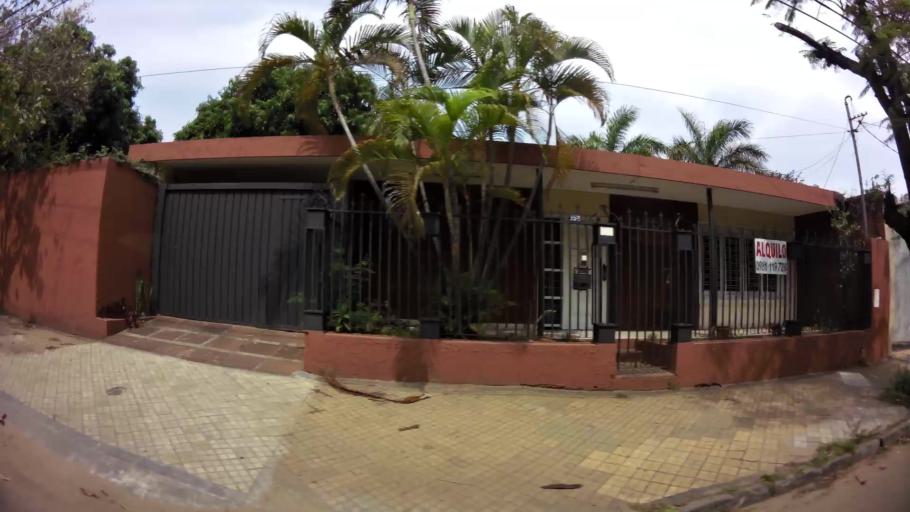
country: PY
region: Asuncion
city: Asuncion
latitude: -25.2891
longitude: -57.5857
